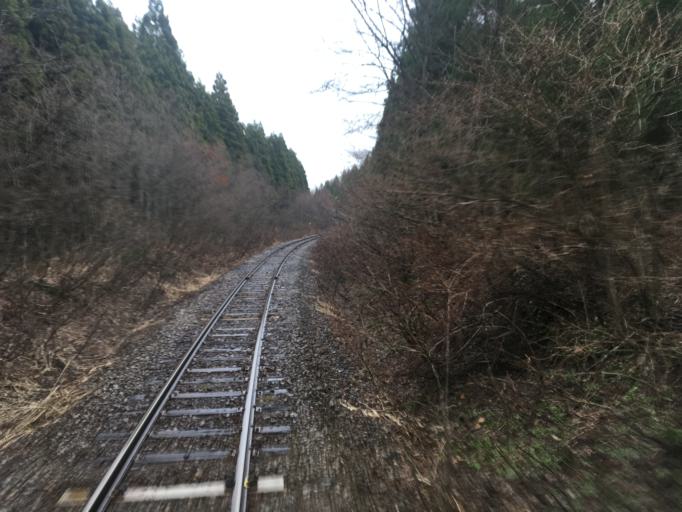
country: JP
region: Akita
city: Takanosu
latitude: 40.1842
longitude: 140.3335
